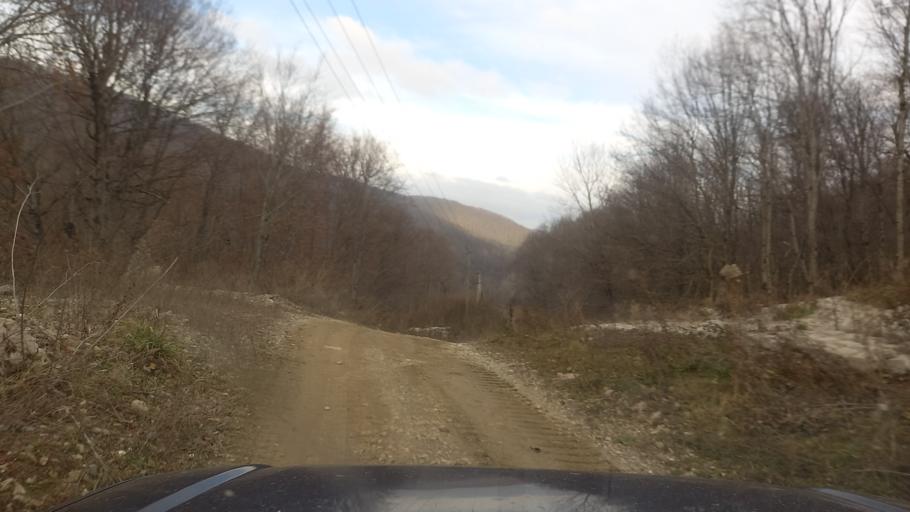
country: RU
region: Krasnodarskiy
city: Neftegorsk
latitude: 44.2135
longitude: 39.7121
